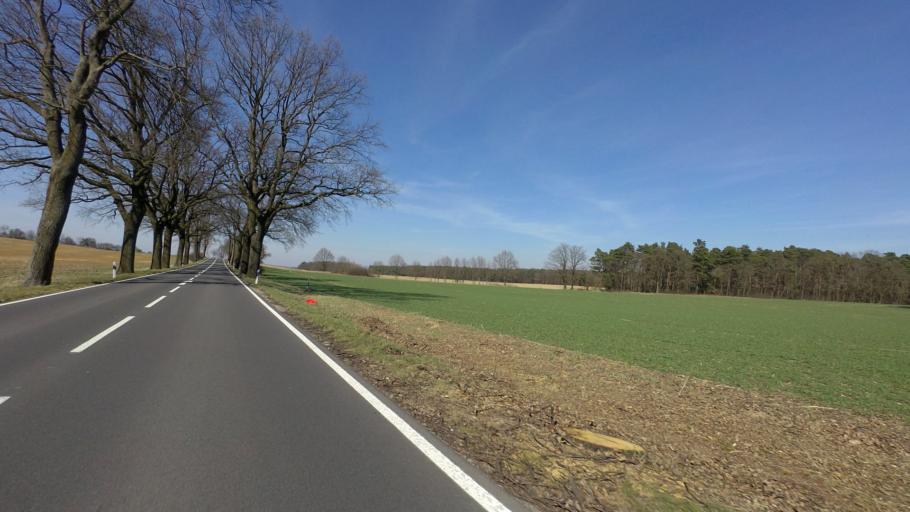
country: DE
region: Brandenburg
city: Waldsieversdorf
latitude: 52.5674
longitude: 14.0355
